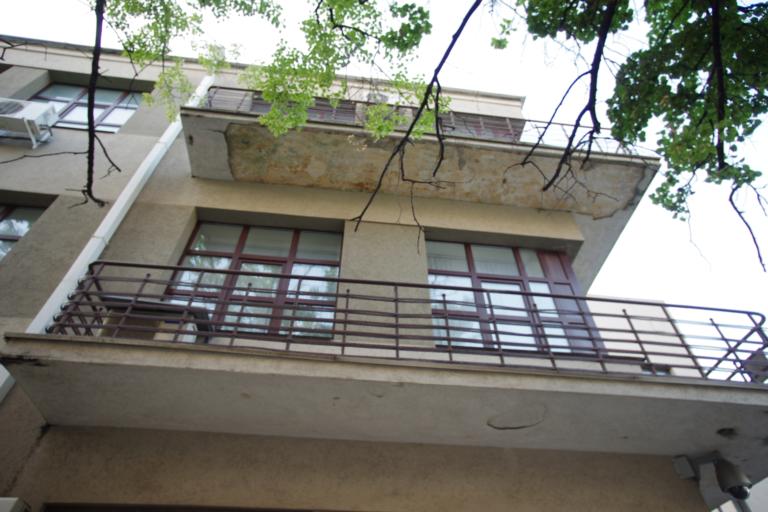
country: RU
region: Nizjnij Novgorod
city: Nizhniy Novgorod
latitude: 56.3205
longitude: 44.0014
